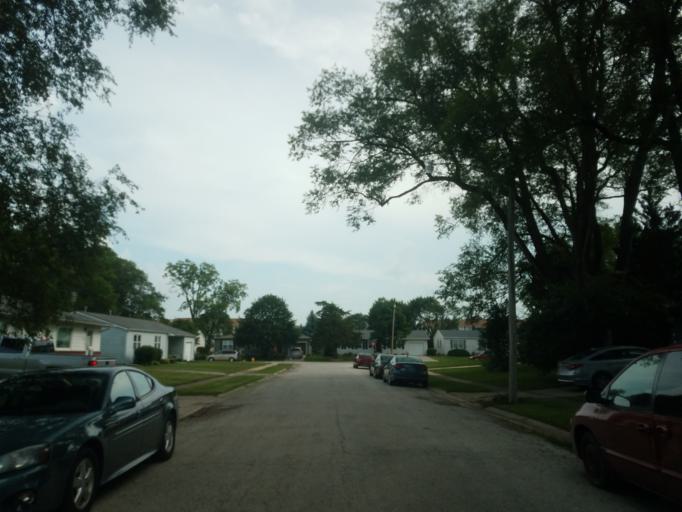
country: US
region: Illinois
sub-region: McLean County
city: Bloomington
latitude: 40.4641
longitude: -88.9678
